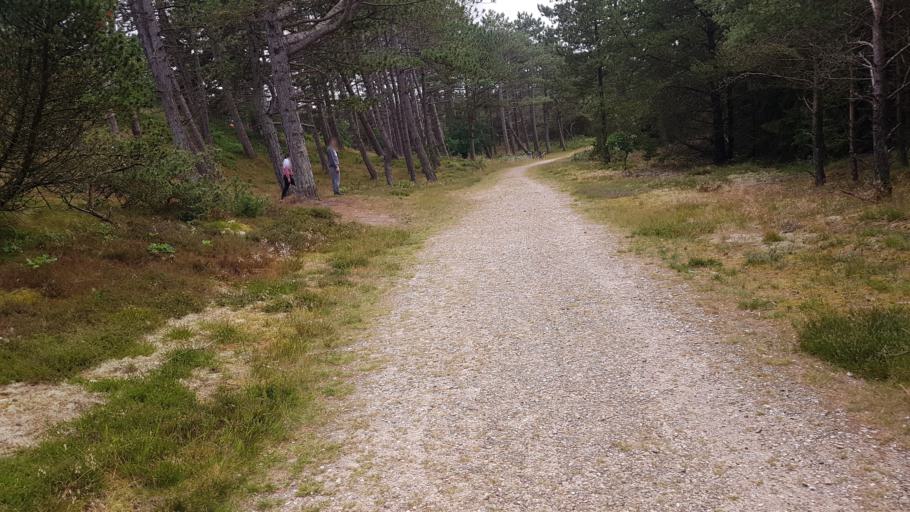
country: DE
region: Schleswig-Holstein
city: List
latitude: 55.1031
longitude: 8.5289
